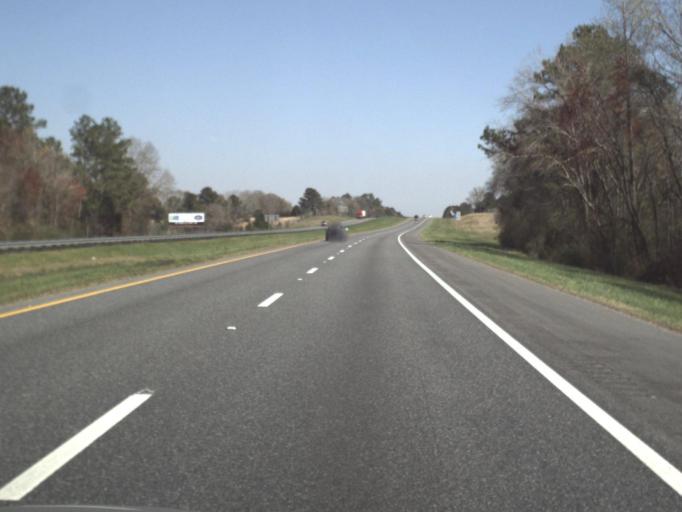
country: US
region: Florida
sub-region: Jackson County
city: Marianna
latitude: 30.7546
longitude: -85.3711
